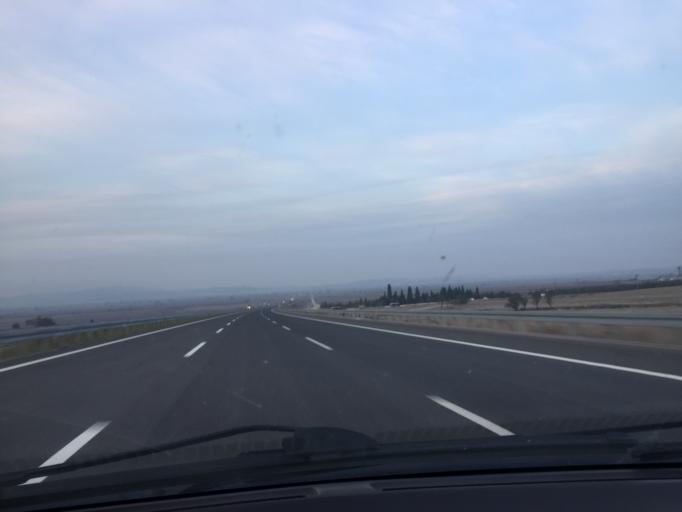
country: TR
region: Manisa
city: Halitpasa
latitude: 38.7000
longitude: 27.6432
